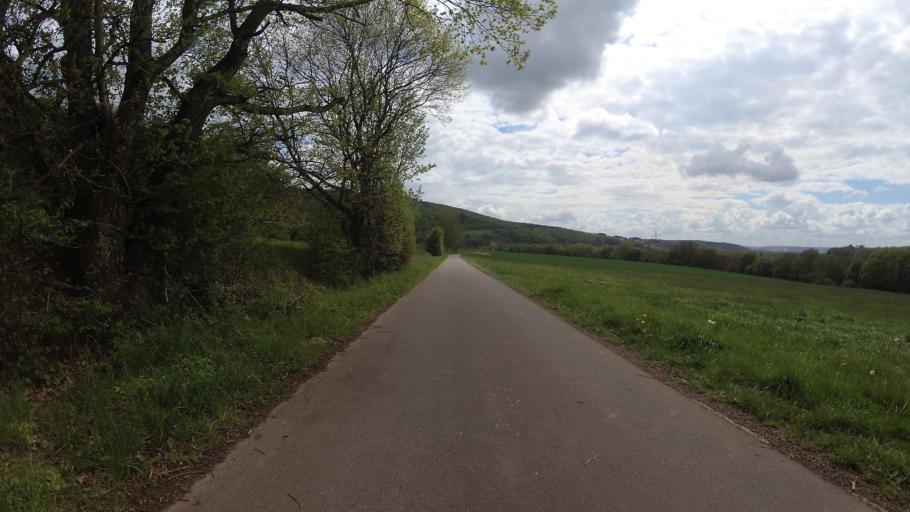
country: DE
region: Saarland
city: Schmelz
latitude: 49.4030
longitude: 6.8586
